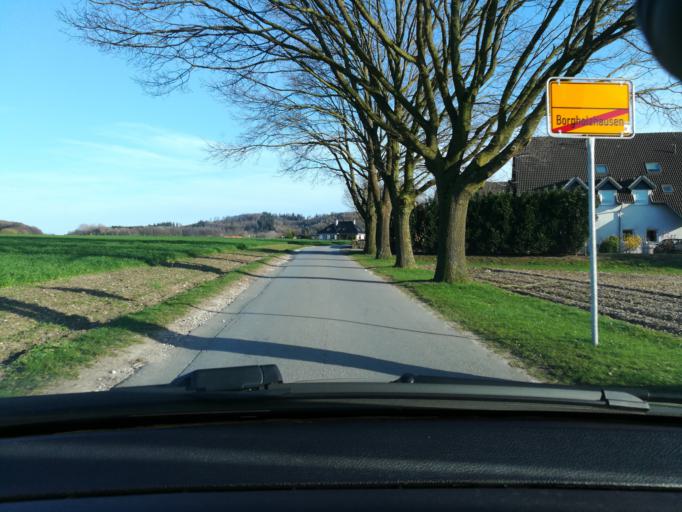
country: DE
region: North Rhine-Westphalia
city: Borgholzhausen
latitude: 52.0956
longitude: 8.2990
